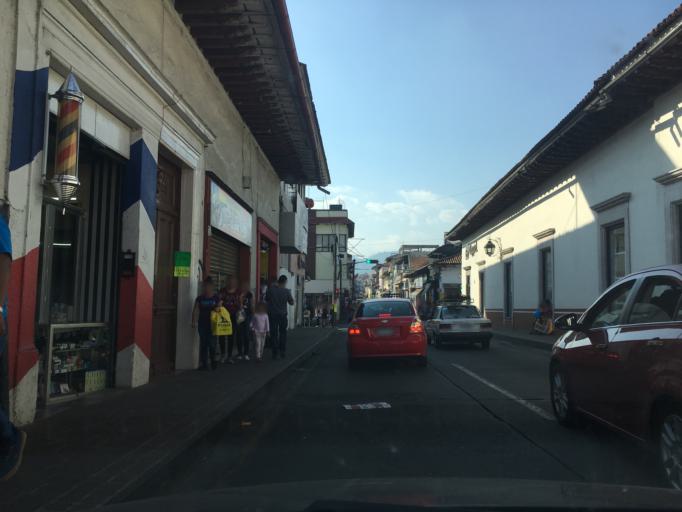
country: MX
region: Michoacan
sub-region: Uruapan
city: Uruapan
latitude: 19.4196
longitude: -102.0627
